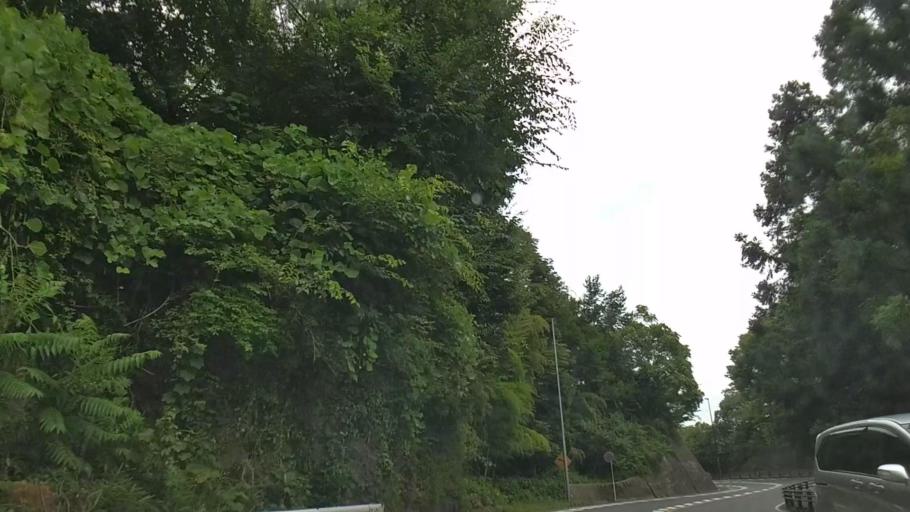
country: JP
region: Yamanashi
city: Uenohara
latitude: 35.6196
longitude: 139.1370
